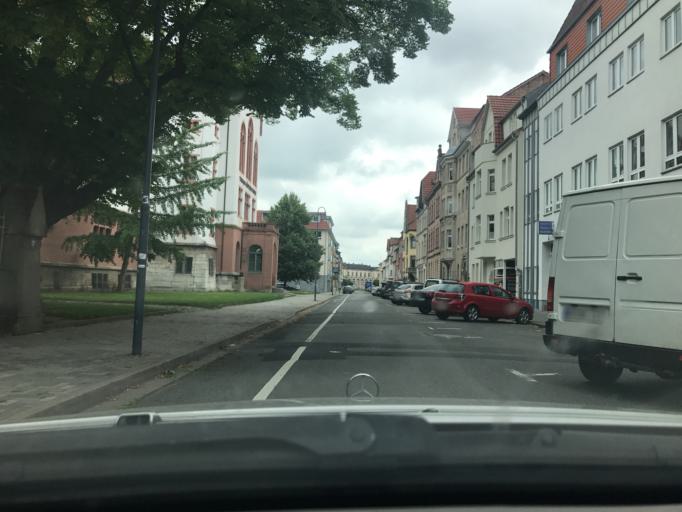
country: DE
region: Thuringia
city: Muehlhausen
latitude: 51.2095
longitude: 10.4690
